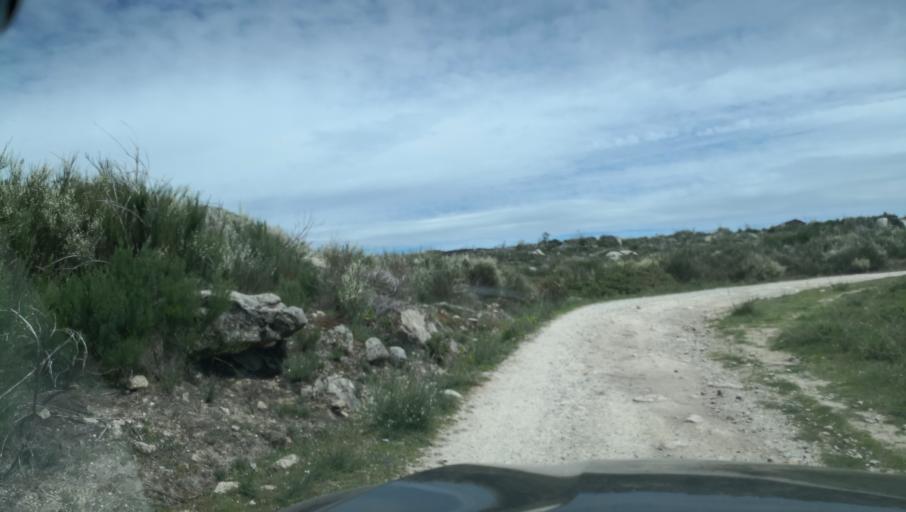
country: PT
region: Vila Real
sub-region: Vila Real
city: Vila Real
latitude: 41.3767
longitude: -7.6586
